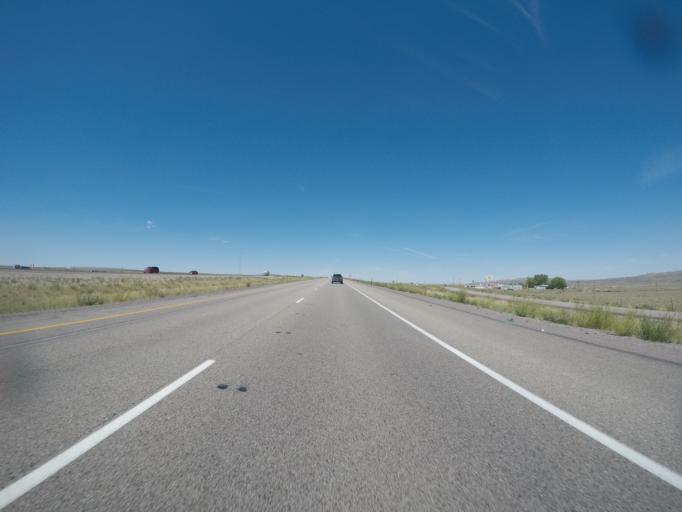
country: US
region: Wyoming
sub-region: Carbon County
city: Saratoga
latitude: 41.7414
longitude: -106.8269
